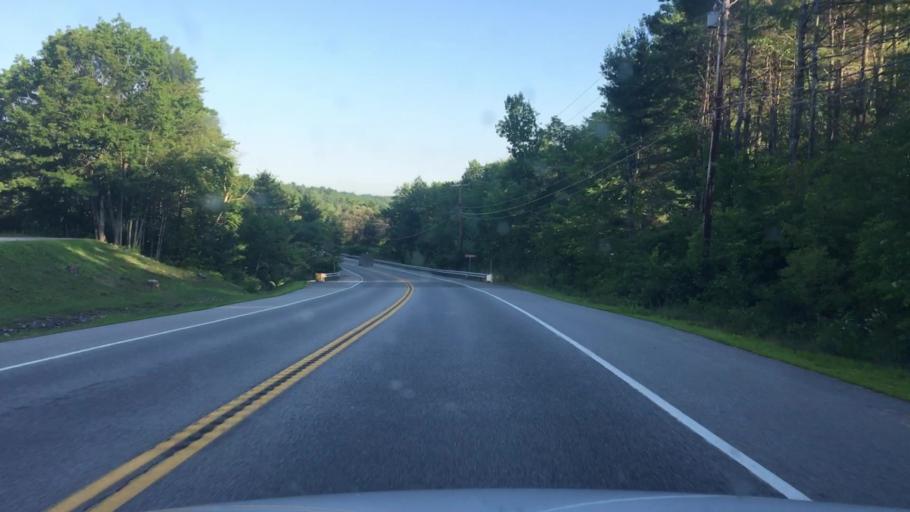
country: US
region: Maine
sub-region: Androscoggin County
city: Lisbon
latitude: 44.0144
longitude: -70.0899
